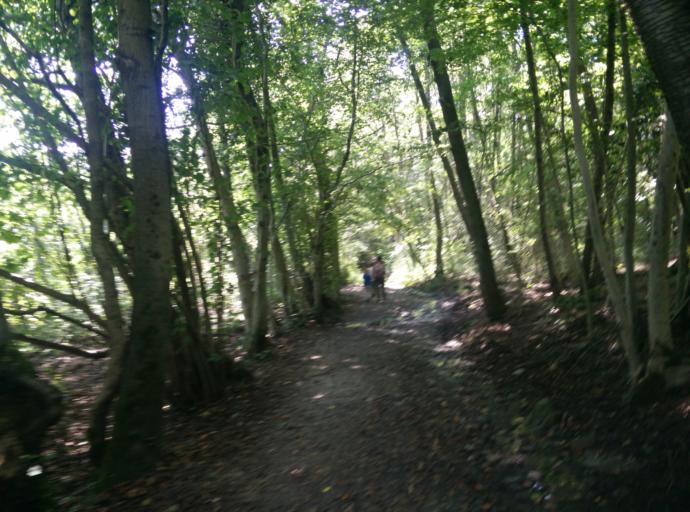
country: IT
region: Piedmont
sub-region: Provincia di Torino
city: Avigliana
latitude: 45.0556
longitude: 7.3847
